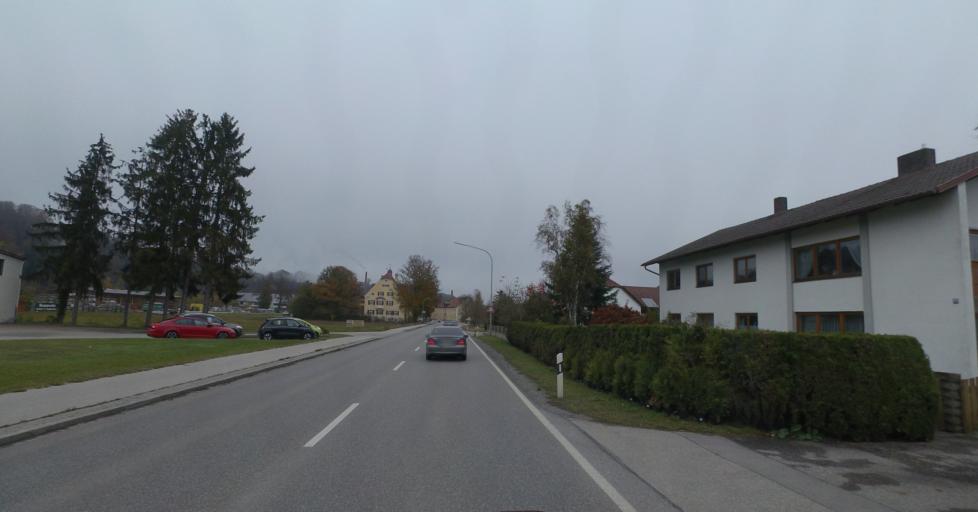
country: DE
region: Bavaria
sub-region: Upper Bavaria
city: Engelsberg
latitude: 48.1033
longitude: 12.5647
